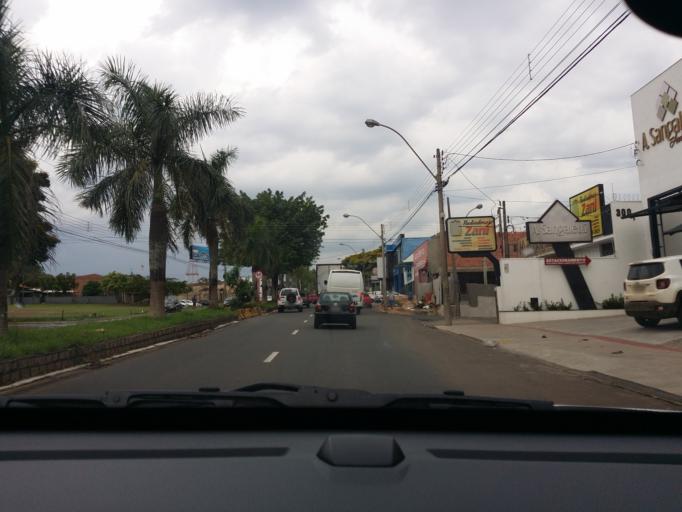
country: BR
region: Sao Paulo
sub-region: Sao Carlos
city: Sao Carlos
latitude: -22.0327
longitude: -47.8868
